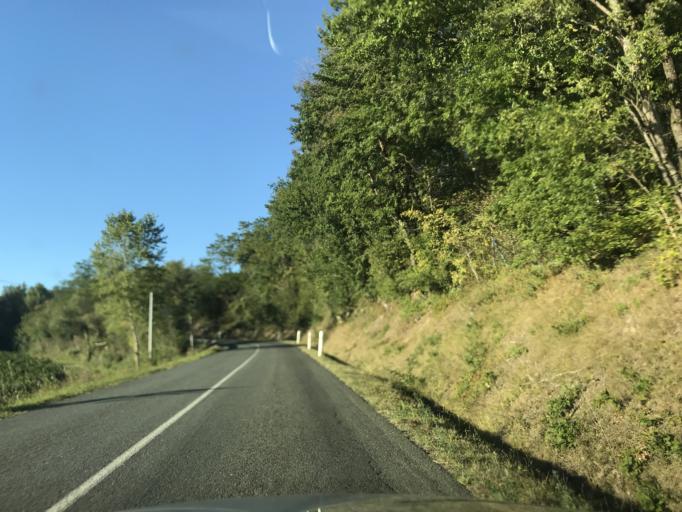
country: FR
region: Aquitaine
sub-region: Departement de la Gironde
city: Rauzan
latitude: 44.7766
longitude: -0.0599
